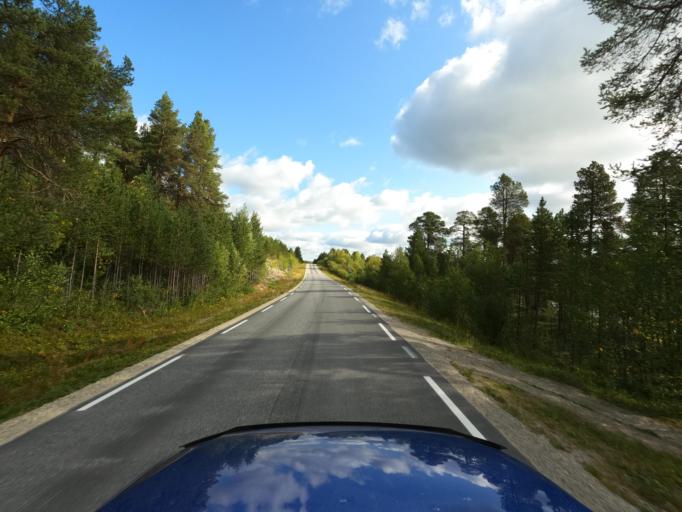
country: NO
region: Finnmark Fylke
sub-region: Karasjok
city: Karasjohka
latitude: 69.4293
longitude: 25.1091
